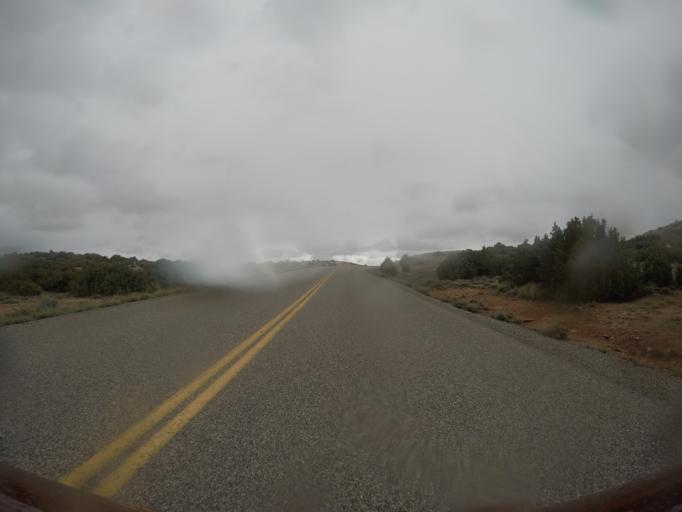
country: US
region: Wyoming
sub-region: Big Horn County
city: Lovell
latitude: 45.0247
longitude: -108.2572
